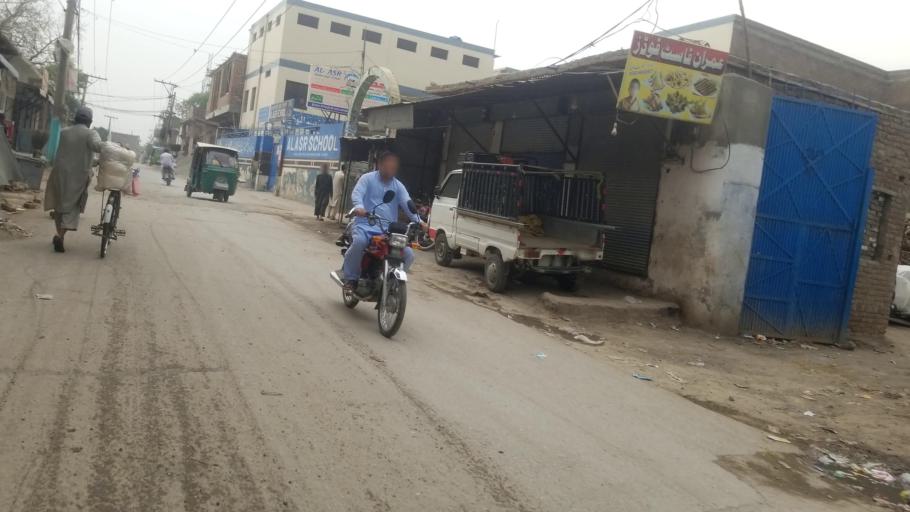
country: PK
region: Khyber Pakhtunkhwa
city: Peshawar
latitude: 33.9894
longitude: 71.5495
